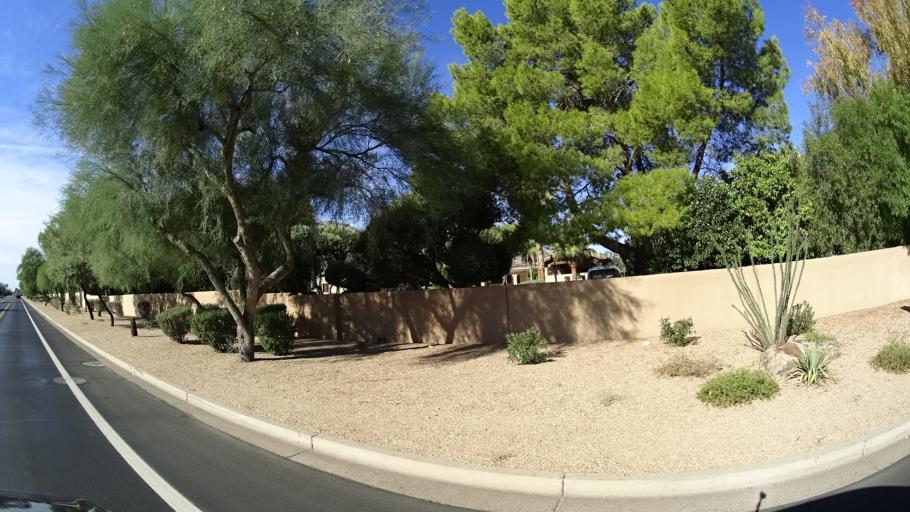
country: US
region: Arizona
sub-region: Maricopa County
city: Paradise Valley
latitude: 33.5294
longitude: -111.9431
